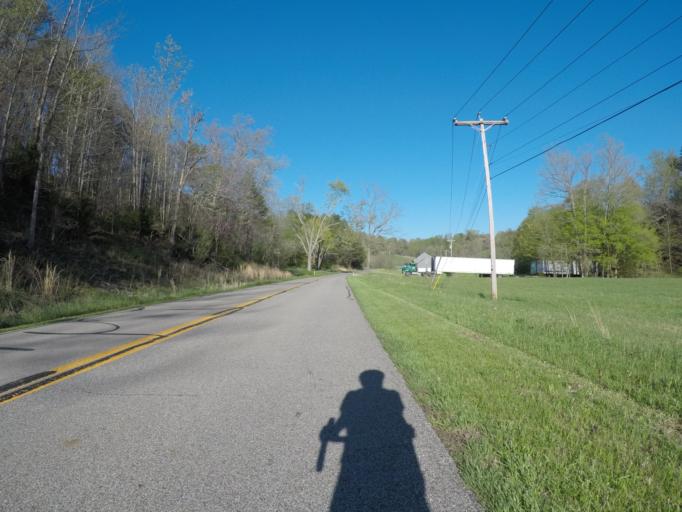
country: US
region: Kentucky
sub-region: Boyd County
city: Meads
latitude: 38.3634
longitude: -82.6748
